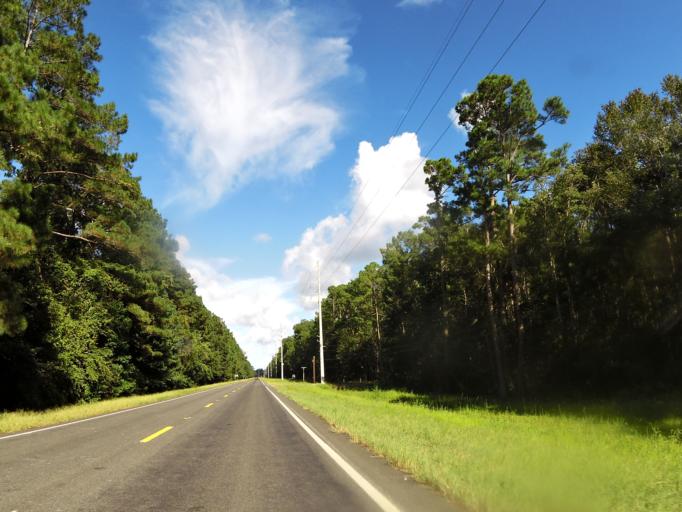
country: US
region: Georgia
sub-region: Glynn County
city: Brunswick
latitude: 31.1063
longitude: -81.6431
